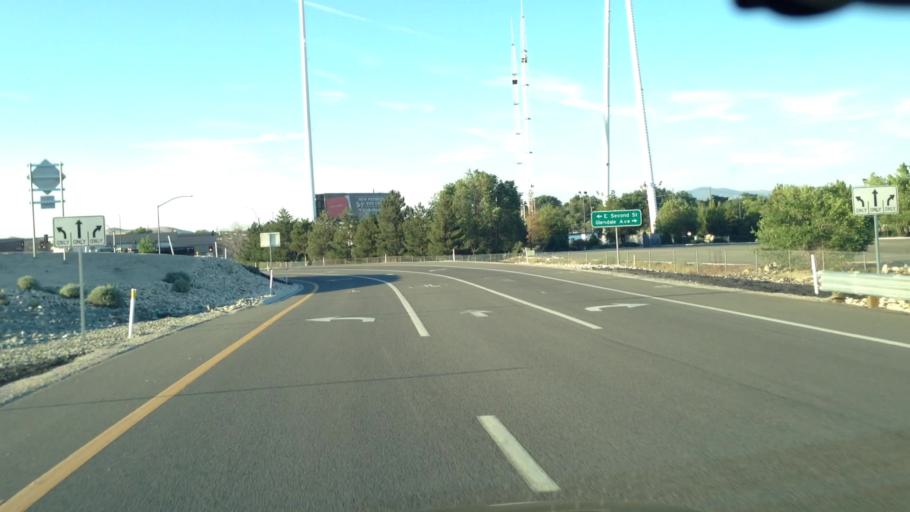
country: US
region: Nevada
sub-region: Washoe County
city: Reno
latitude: 39.5259
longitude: -119.7829
